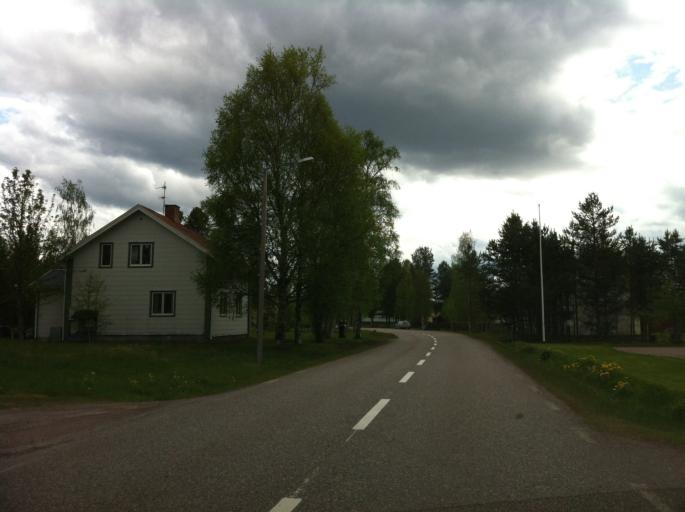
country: NO
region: Hedmark
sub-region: Trysil
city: Innbygda
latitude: 61.4105
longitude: 13.0834
